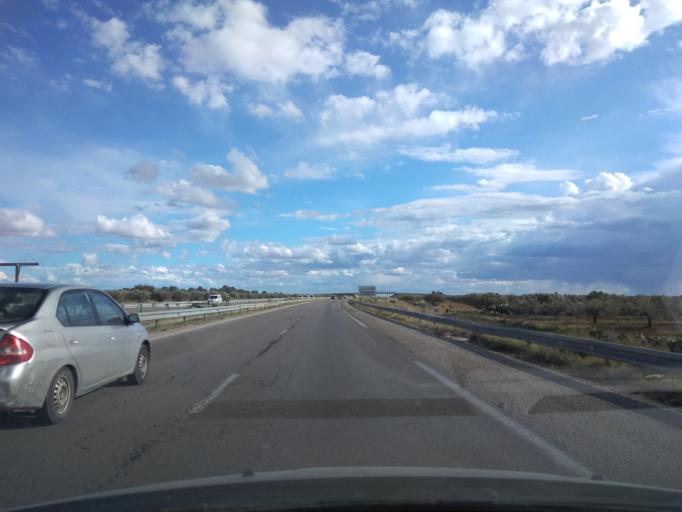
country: TN
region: Al Munastir
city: Manzil Kamil
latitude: 35.6252
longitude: 10.5924
